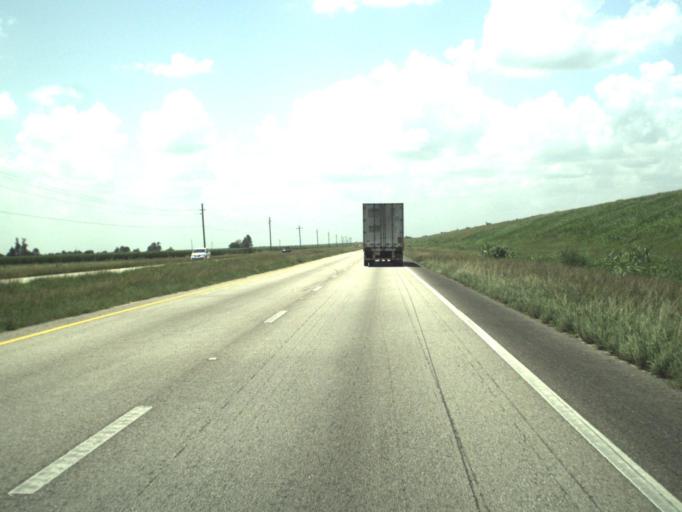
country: US
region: Florida
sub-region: Palm Beach County
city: South Bay
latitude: 26.6886
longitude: -80.7628
